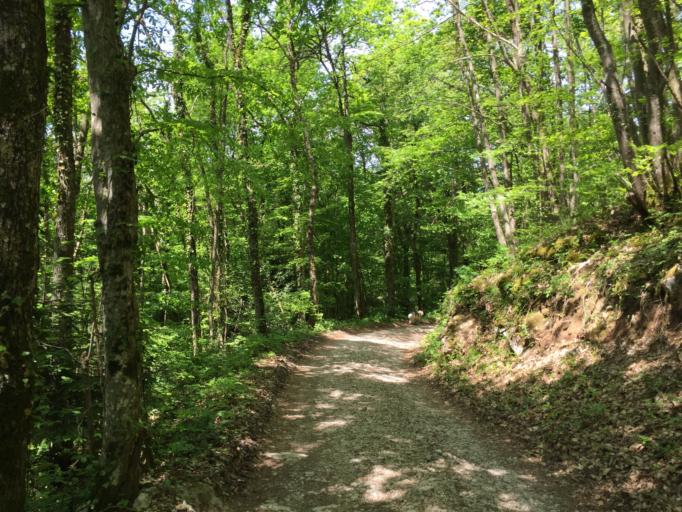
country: FR
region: Rhone-Alpes
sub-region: Departement de la Savoie
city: Mouxy
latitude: 45.6650
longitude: 5.9496
